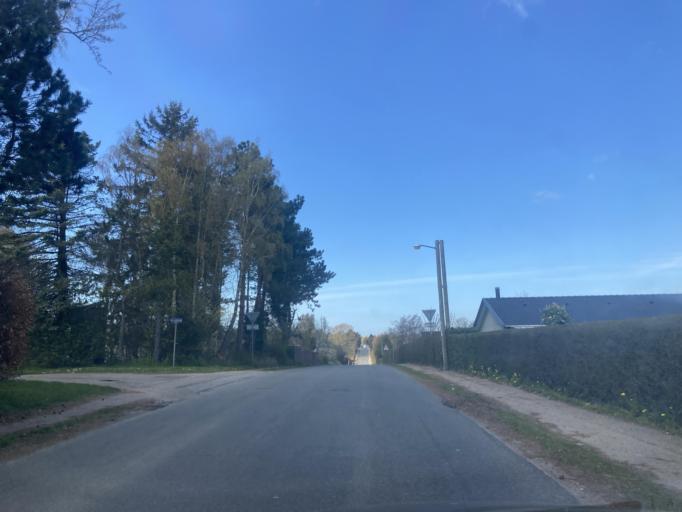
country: DK
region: Capital Region
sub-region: Gribskov Kommune
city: Helsinge
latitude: 56.0623
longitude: 12.1153
